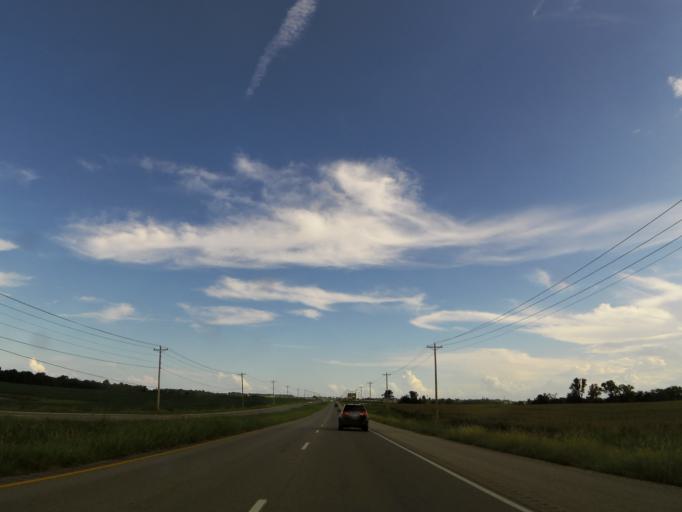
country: US
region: Kentucky
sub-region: Christian County
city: Oak Grove
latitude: 36.7195
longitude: -87.4600
